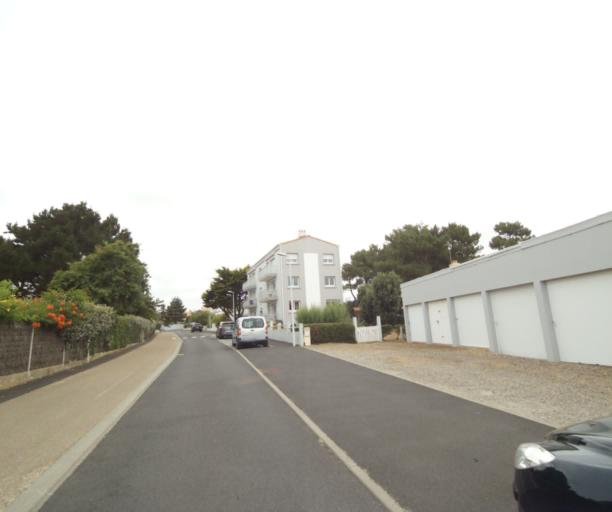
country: FR
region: Pays de la Loire
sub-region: Departement de la Vendee
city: Chateau-d'Olonne
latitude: 46.4744
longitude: -1.7451
